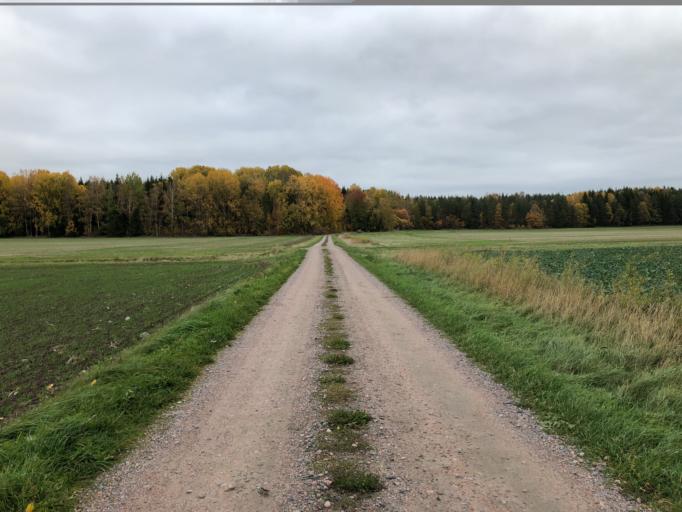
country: SE
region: Soedermanland
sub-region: Oxelosunds Kommun
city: Bara
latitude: 58.7174
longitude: 17.0447
